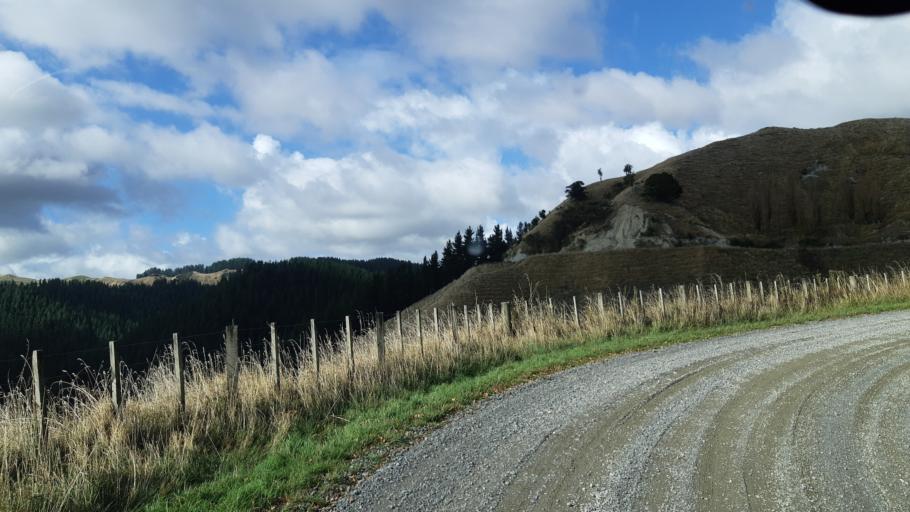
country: NZ
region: Manawatu-Wanganui
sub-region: Ruapehu District
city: Waiouru
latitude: -39.7673
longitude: 175.6754
